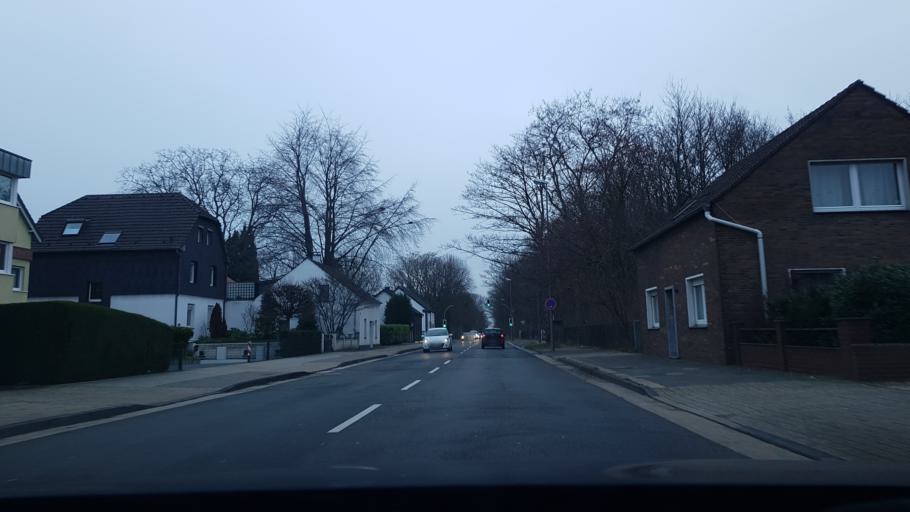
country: DE
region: North Rhine-Westphalia
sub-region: Regierungsbezirk Dusseldorf
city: Moers
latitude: 51.4271
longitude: 6.6509
